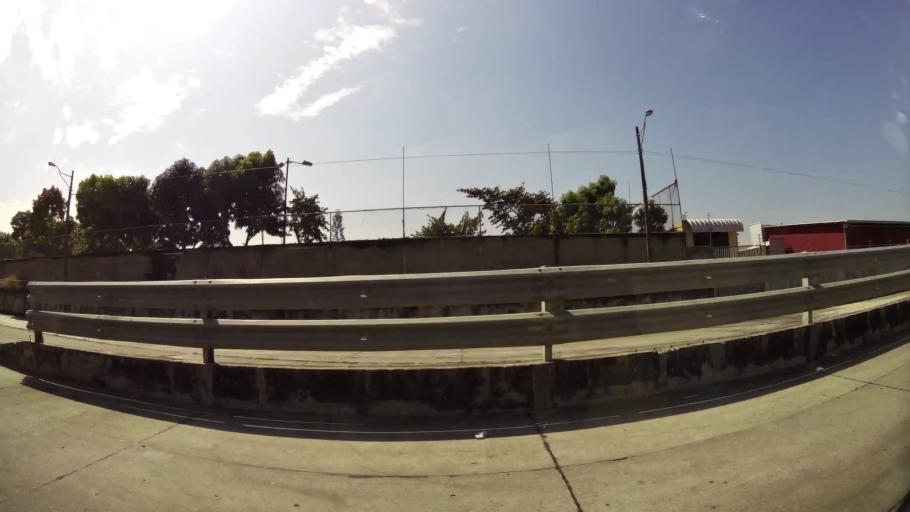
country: EC
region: Guayas
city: Eloy Alfaro
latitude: -2.1233
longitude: -79.9069
